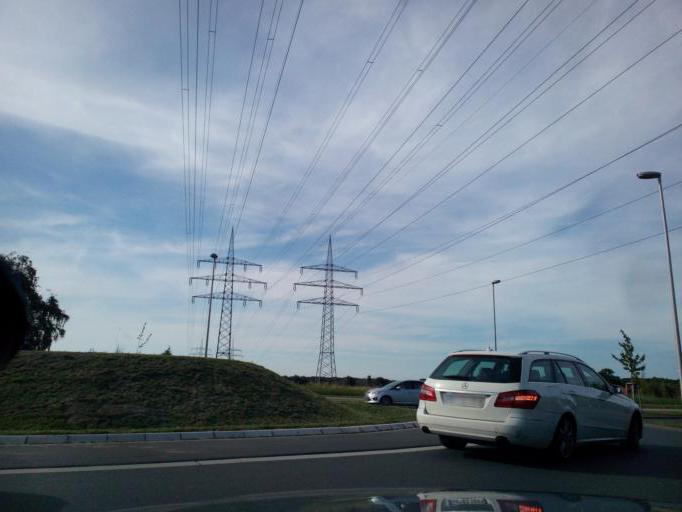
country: DE
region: North Rhine-Westphalia
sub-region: Regierungsbezirk Munster
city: Muenster
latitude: 51.9356
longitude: 7.5846
